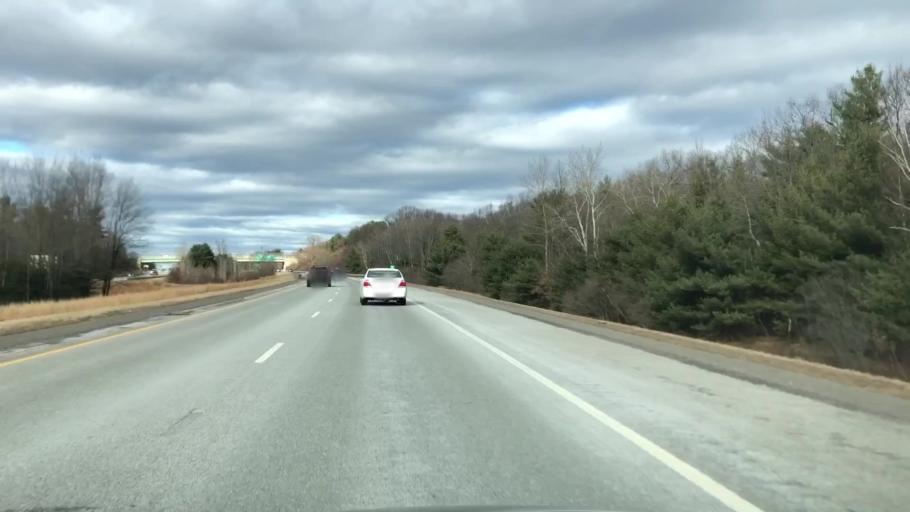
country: US
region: Massachusetts
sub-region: Worcester County
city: Leominster
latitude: 42.5036
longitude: -71.7203
